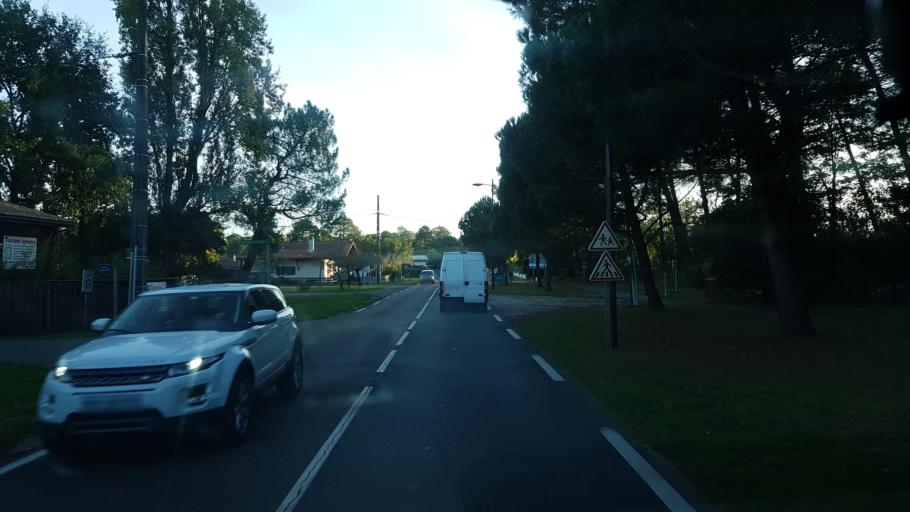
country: FR
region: Aquitaine
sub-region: Departement de la Gironde
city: Ares
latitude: 44.7578
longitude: -1.1801
